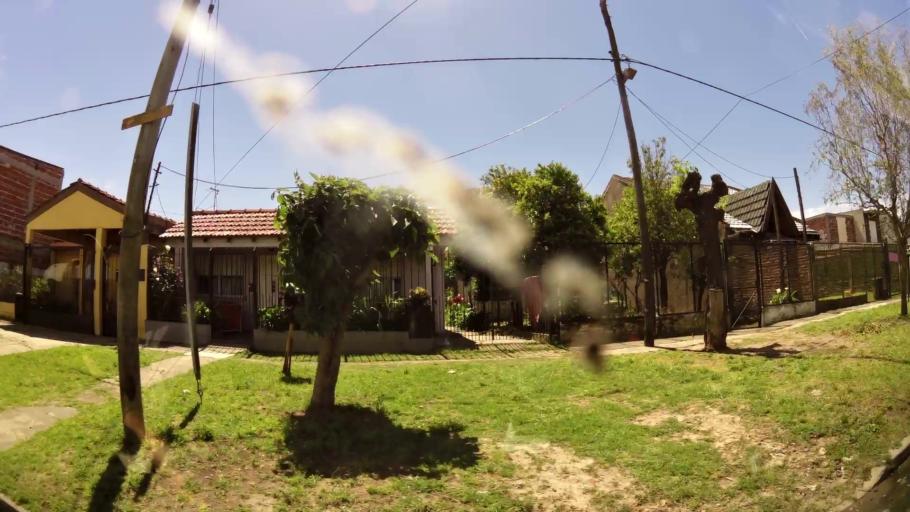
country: AR
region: Buenos Aires
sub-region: Partido de Quilmes
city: Quilmes
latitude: -34.7355
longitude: -58.3044
